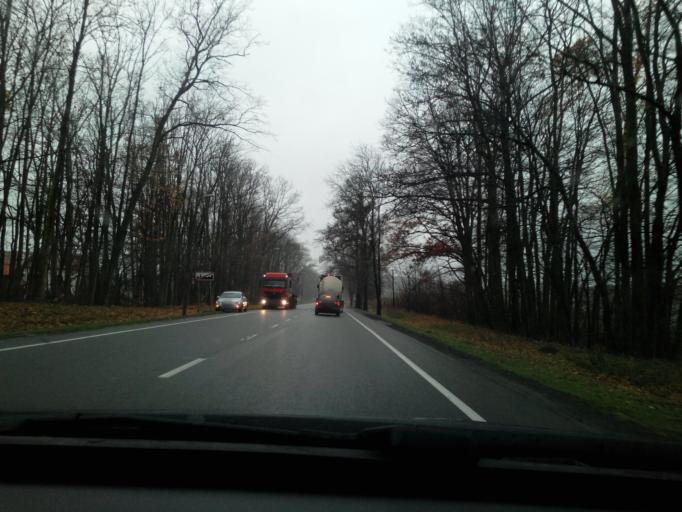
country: PL
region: Pomeranian Voivodeship
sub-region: Powiat tczewski
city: Subkowy
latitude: 54.0460
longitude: 18.7300
